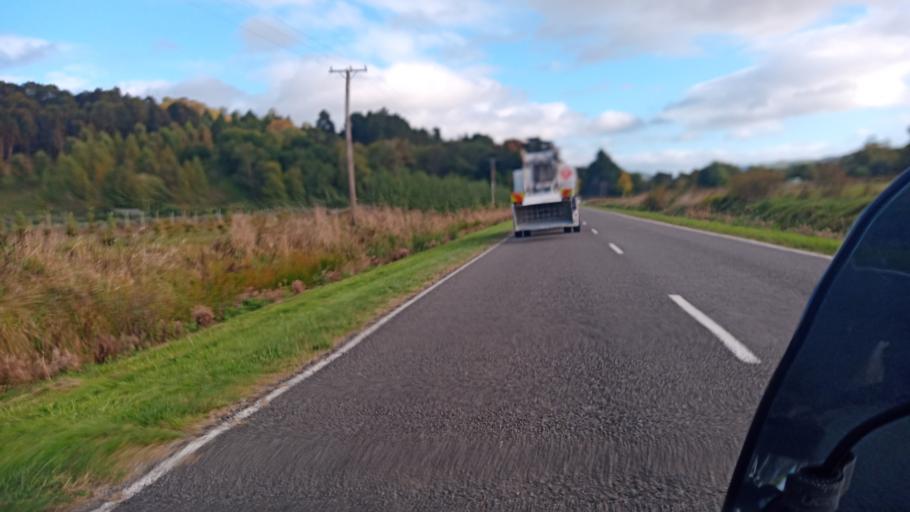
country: NZ
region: Gisborne
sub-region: Gisborne District
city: Gisborne
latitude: -38.6006
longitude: 177.8035
